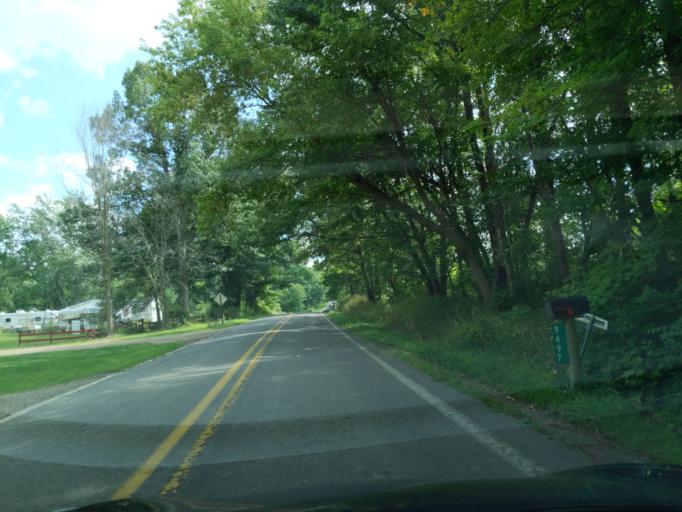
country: US
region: Michigan
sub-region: Jackson County
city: Spring Arbor
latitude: 42.3421
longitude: -84.5506
